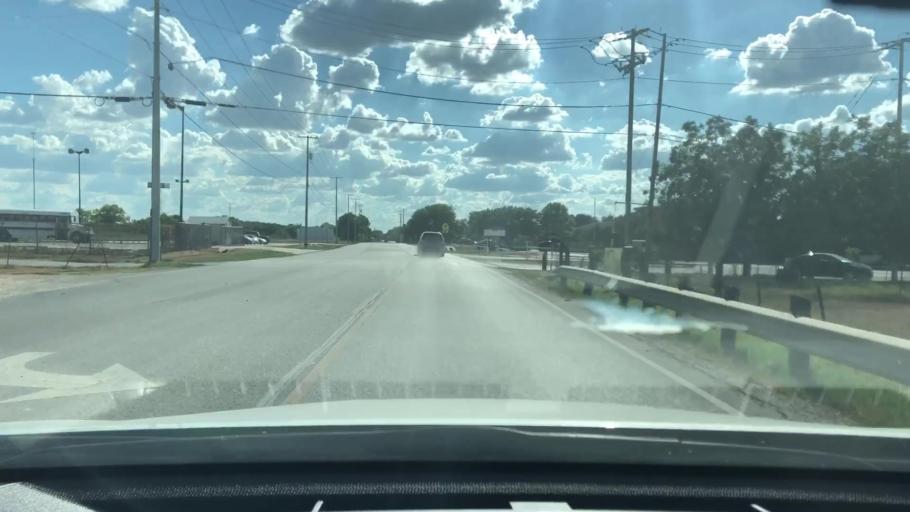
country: US
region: Texas
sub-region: Guadalupe County
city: Northcliff
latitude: 29.6444
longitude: -98.2256
